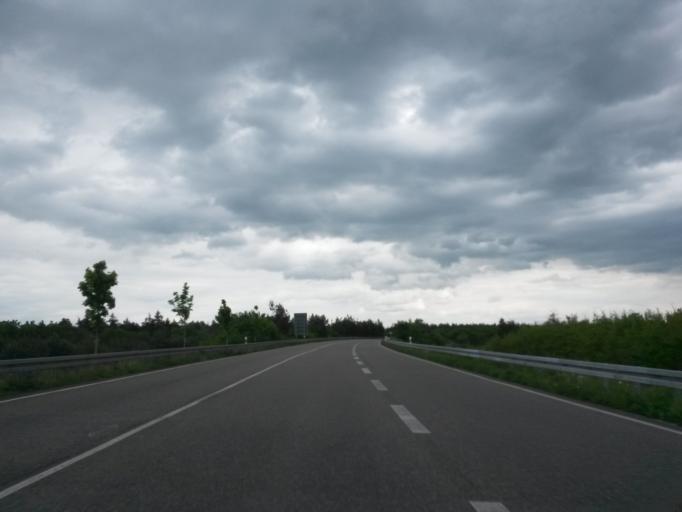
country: DE
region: Baden-Wuerttemberg
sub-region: Karlsruhe Region
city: Hambrucken
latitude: 49.2001
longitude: 8.5092
